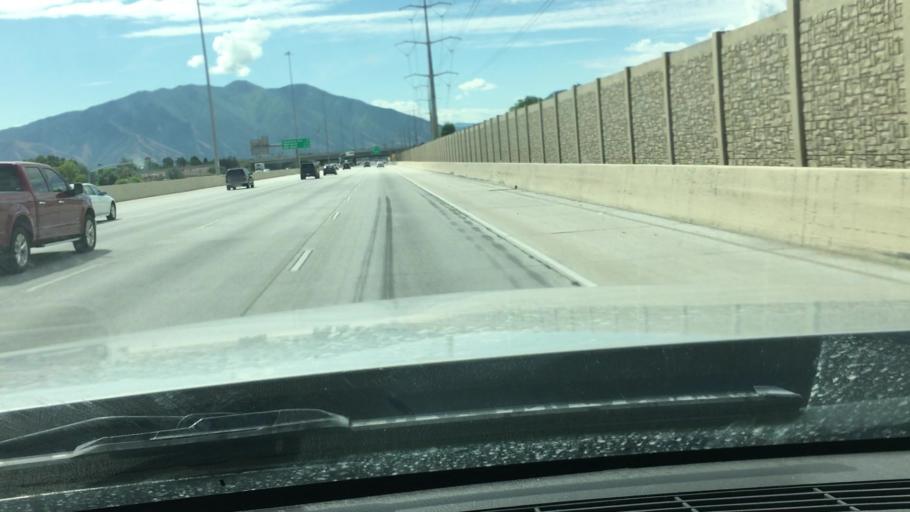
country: US
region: Utah
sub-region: Utah County
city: Provo
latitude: 40.2137
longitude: -111.6636
